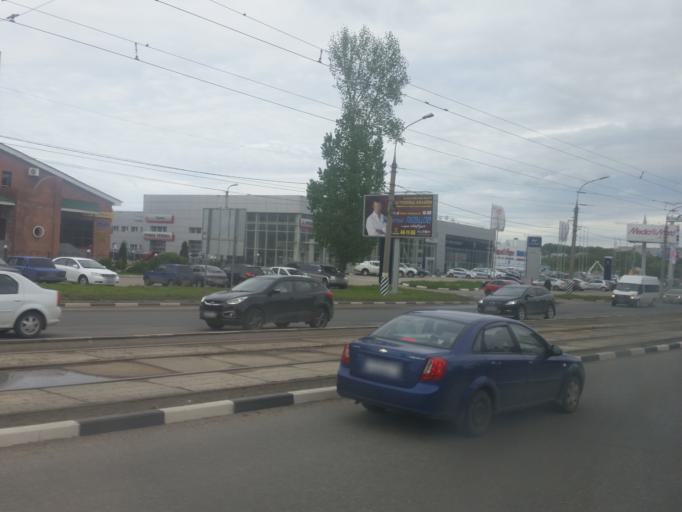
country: RU
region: Ulyanovsk
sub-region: Ulyanovskiy Rayon
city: Ulyanovsk
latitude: 54.3051
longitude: 48.3546
